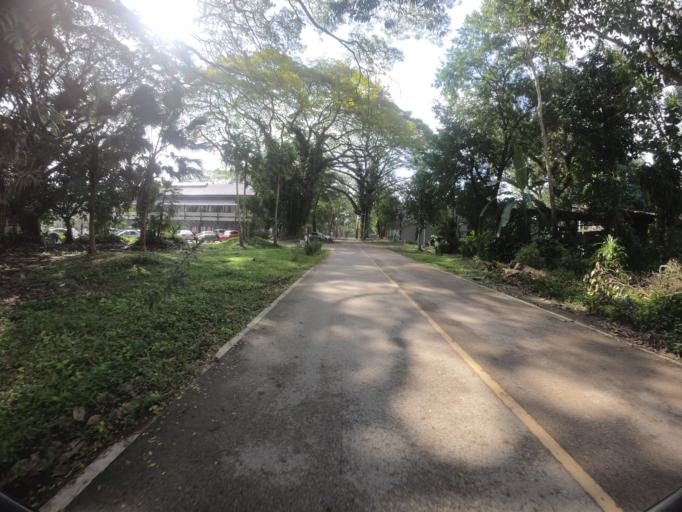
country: TH
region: Chiang Mai
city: Chiang Mai
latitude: 18.7960
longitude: 98.9503
